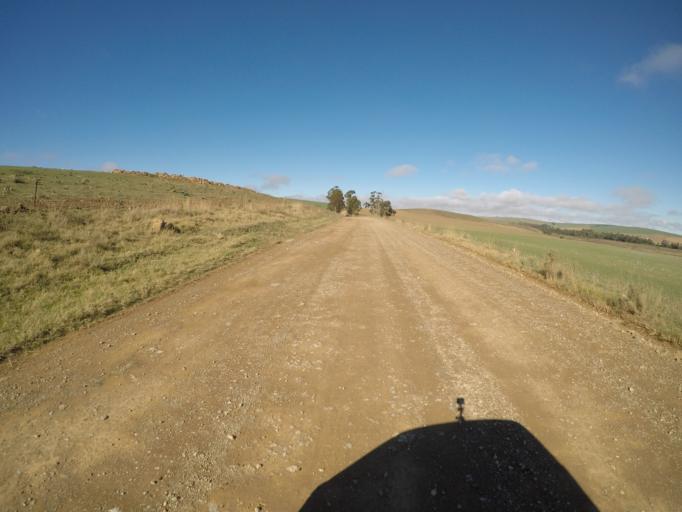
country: ZA
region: Western Cape
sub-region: Overberg District Municipality
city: Caledon
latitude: -34.1089
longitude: 19.7073
